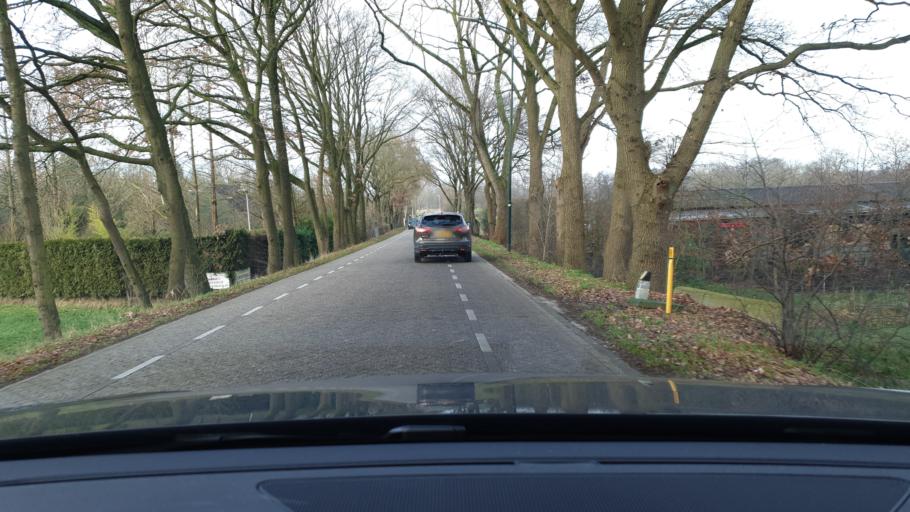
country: NL
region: North Brabant
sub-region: Gemeente Eindhoven
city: Muschberg en Geestenberg
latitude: 51.4319
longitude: 5.5407
